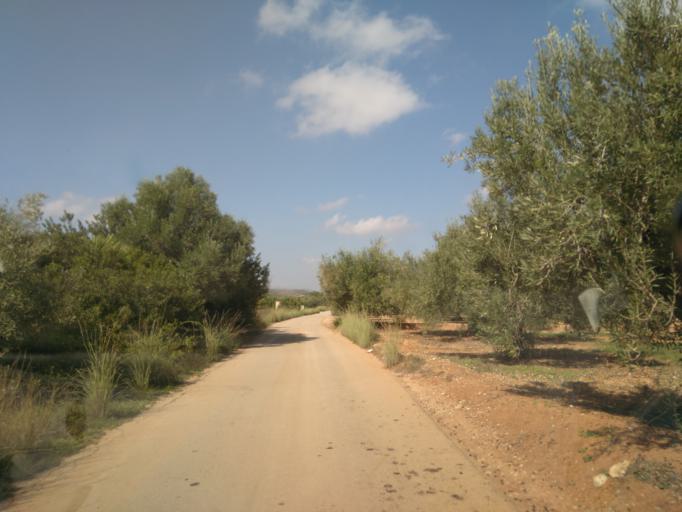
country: ES
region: Valencia
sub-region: Provincia de Valencia
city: Tous
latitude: 39.1720
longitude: -0.5911
